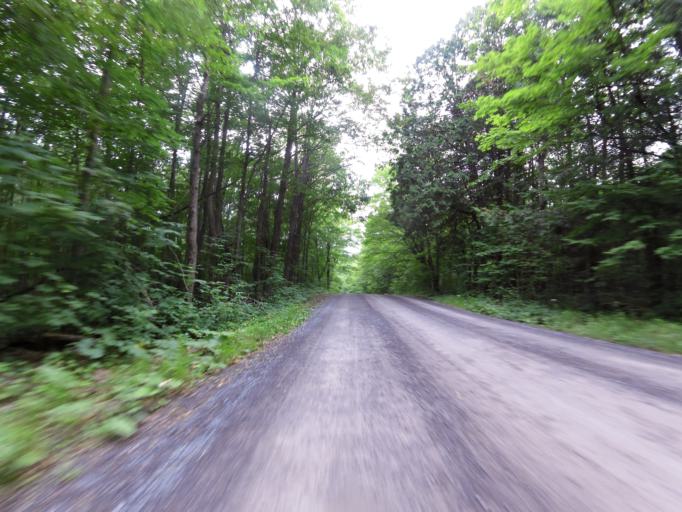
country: CA
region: Ontario
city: Carleton Place
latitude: 45.1484
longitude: -76.2159
